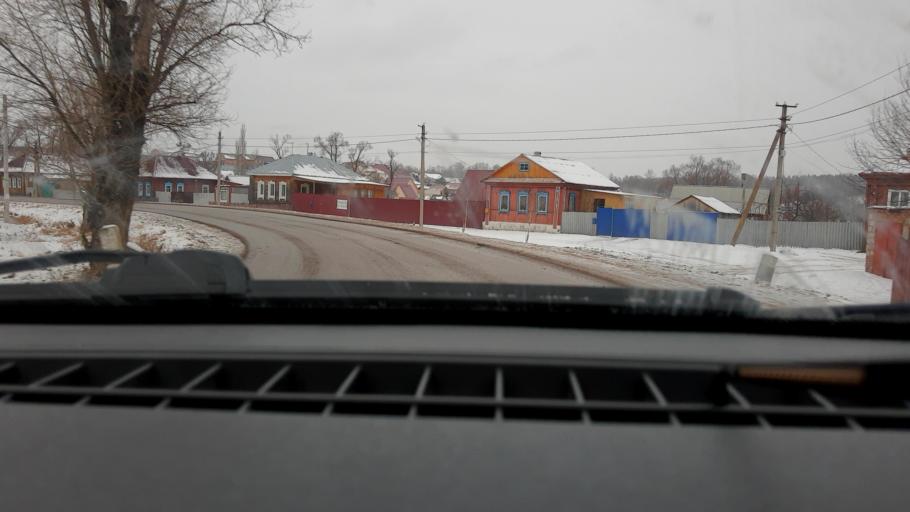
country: RU
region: Bashkortostan
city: Kabakovo
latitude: 54.7043
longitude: 56.2469
